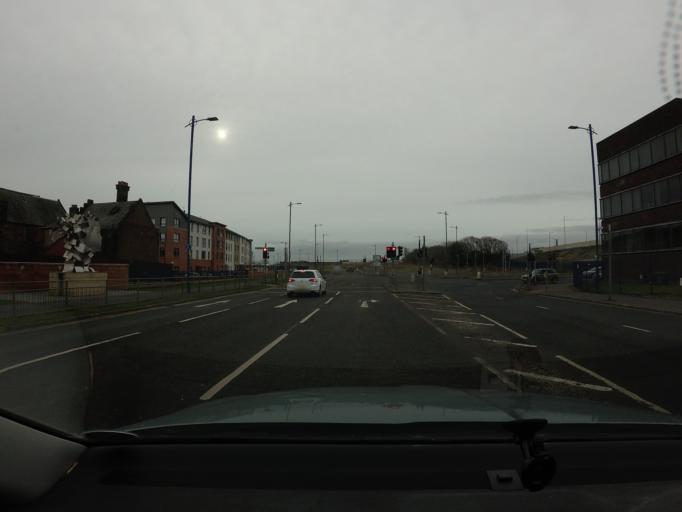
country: GB
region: Scotland
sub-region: South Lanarkshire
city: Rutherglen
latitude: 55.8389
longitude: -4.2400
